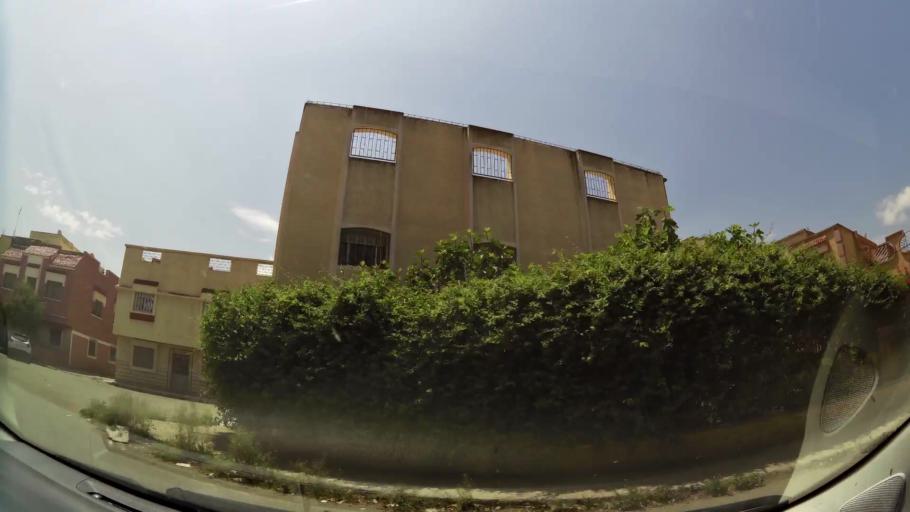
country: MA
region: Oriental
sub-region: Oujda-Angad
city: Oujda
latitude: 34.6900
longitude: -1.8899
